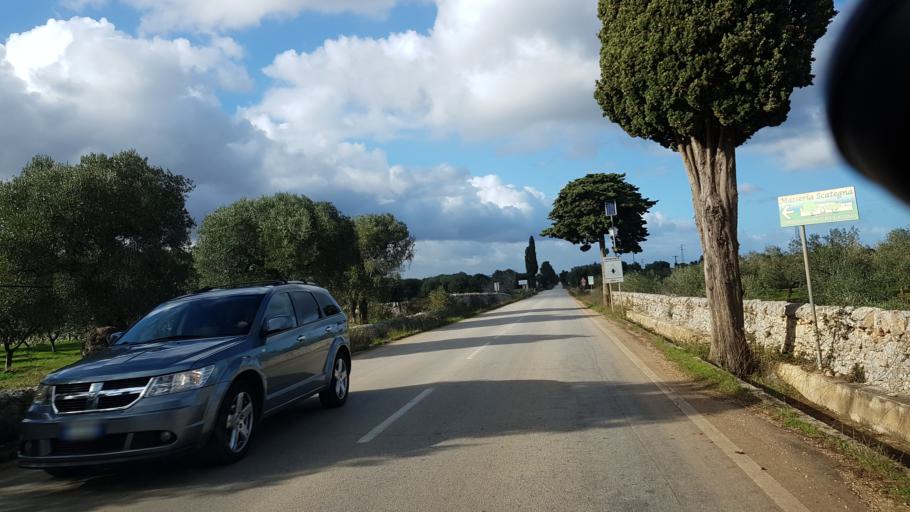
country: IT
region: Apulia
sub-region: Provincia di Brindisi
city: Montalbano
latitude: 40.7724
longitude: 17.5025
